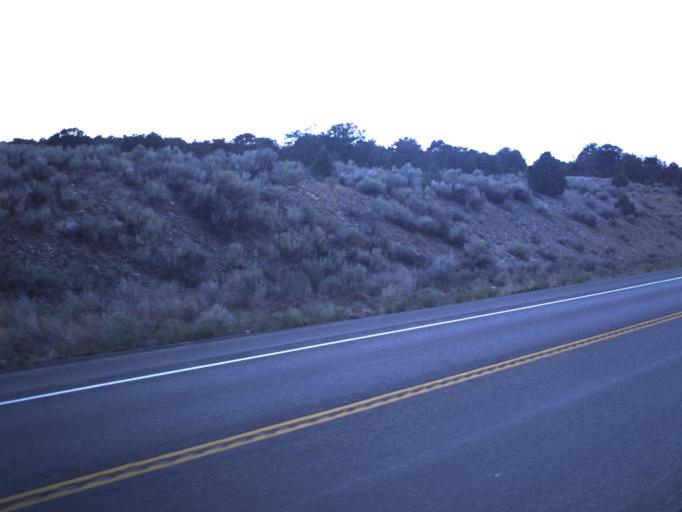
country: US
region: Utah
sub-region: Duchesne County
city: Duchesne
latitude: 40.1779
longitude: -110.5983
